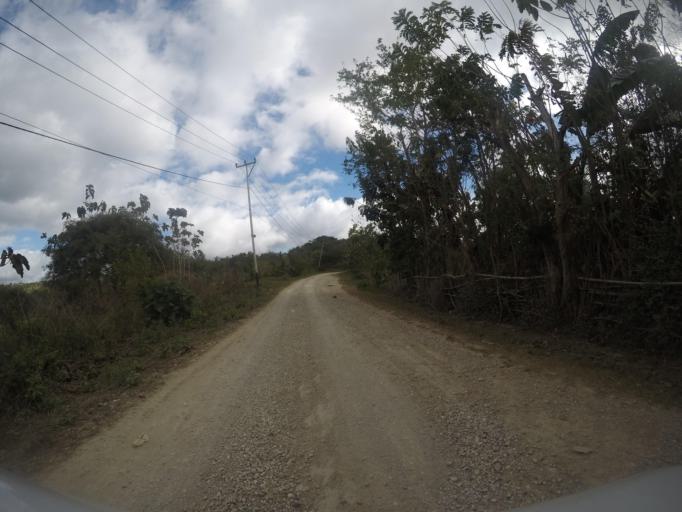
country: TL
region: Lautem
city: Lospalos
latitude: -8.5637
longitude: 126.8882
